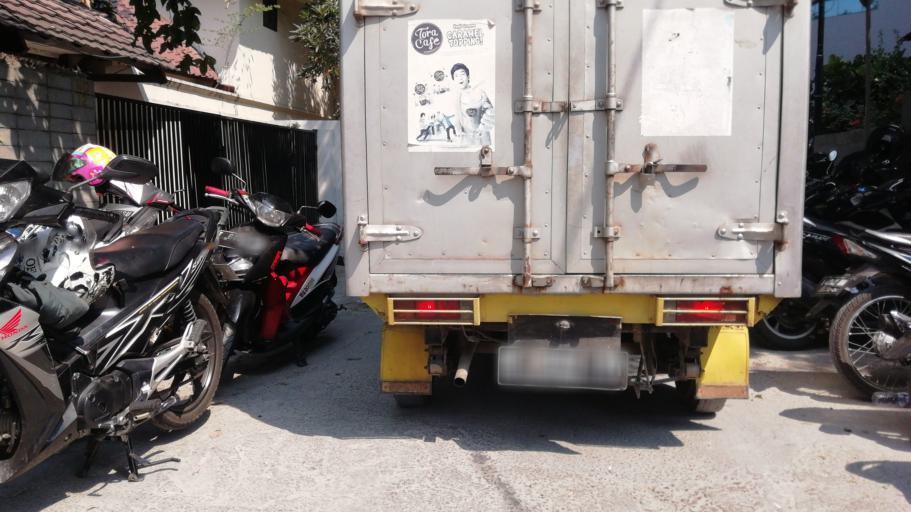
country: ID
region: Jakarta Raya
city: Jakarta
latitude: -6.1983
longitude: 106.8220
